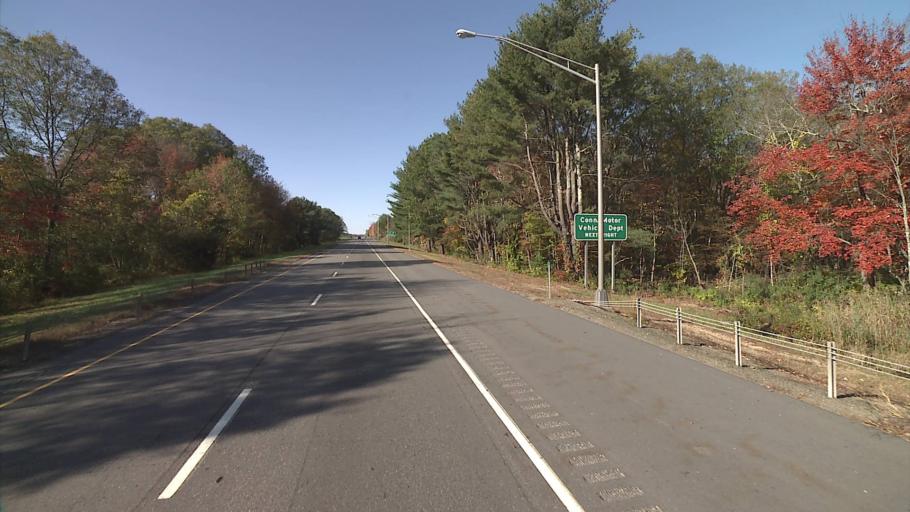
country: US
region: Connecticut
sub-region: Windham County
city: Willimantic
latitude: 41.7296
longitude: -72.2316
